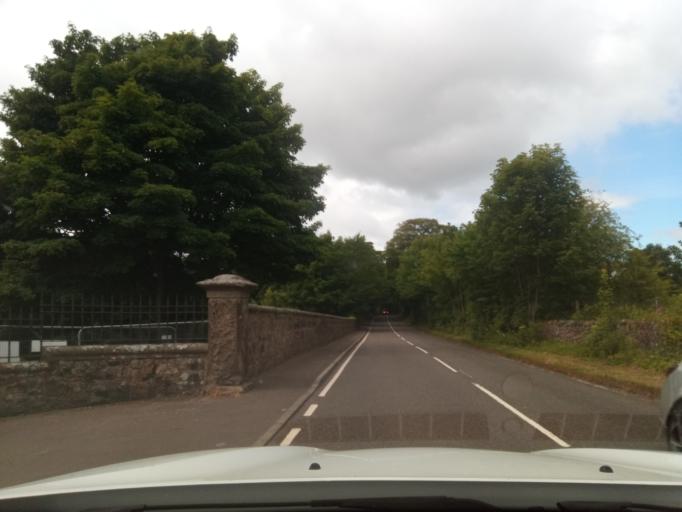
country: GB
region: Scotland
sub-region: Fife
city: Oakley
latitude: 56.0592
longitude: -3.5524
